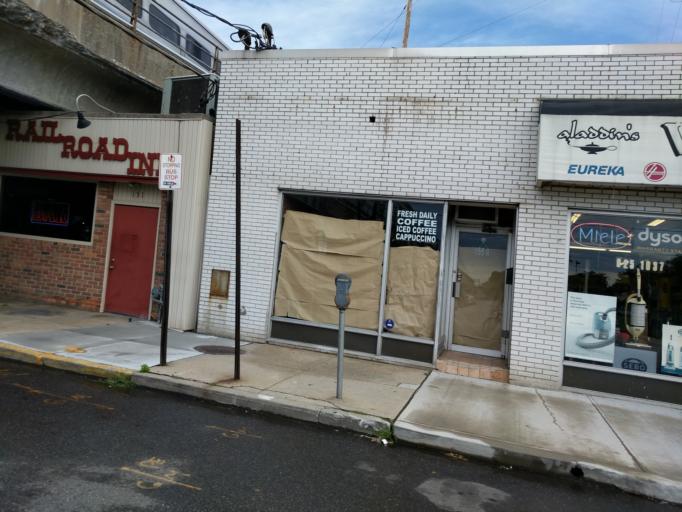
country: US
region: New York
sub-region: Nassau County
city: Valley Stream
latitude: 40.6609
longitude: -73.7032
